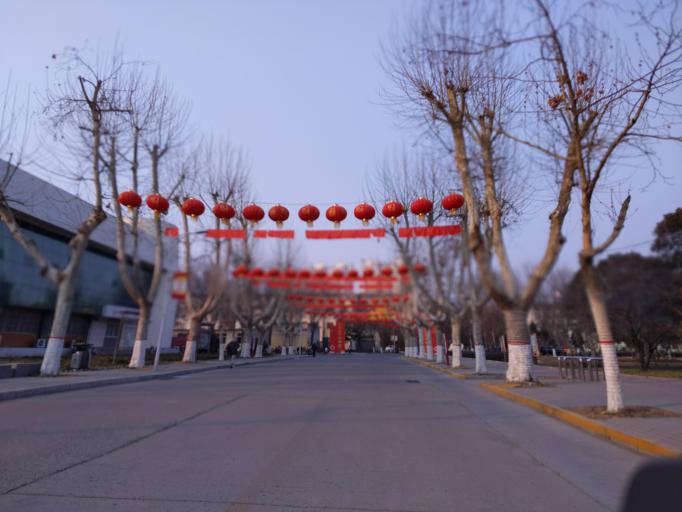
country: CN
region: Henan Sheng
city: Zhongyuanlu
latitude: 35.7803
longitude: 115.0565
